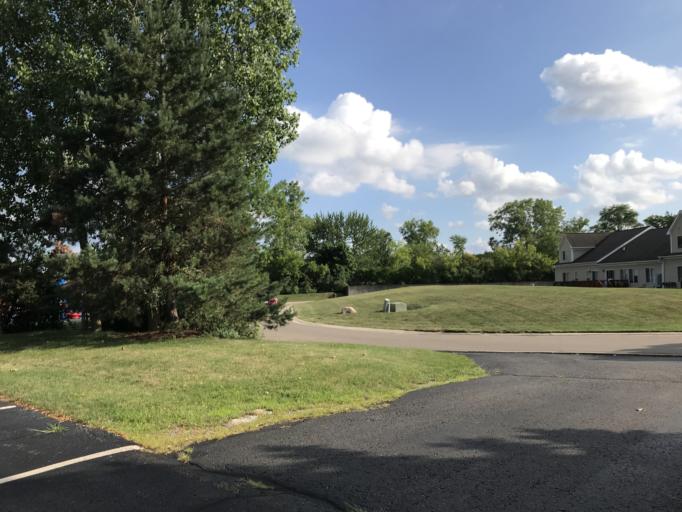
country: US
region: Michigan
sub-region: Oakland County
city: Farmington Hills
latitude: 42.4788
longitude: -83.3397
